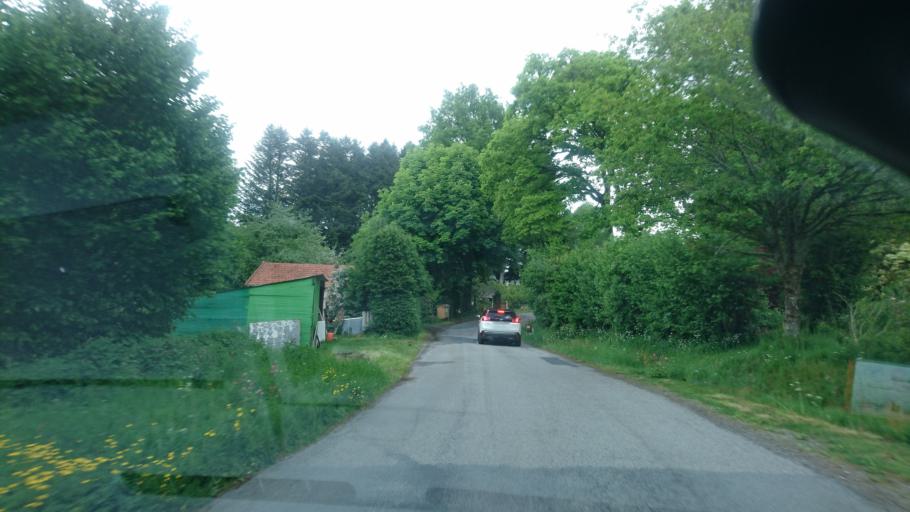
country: FR
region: Limousin
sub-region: Departement de la Haute-Vienne
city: Peyrat-le-Chateau
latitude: 45.7906
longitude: 1.9107
